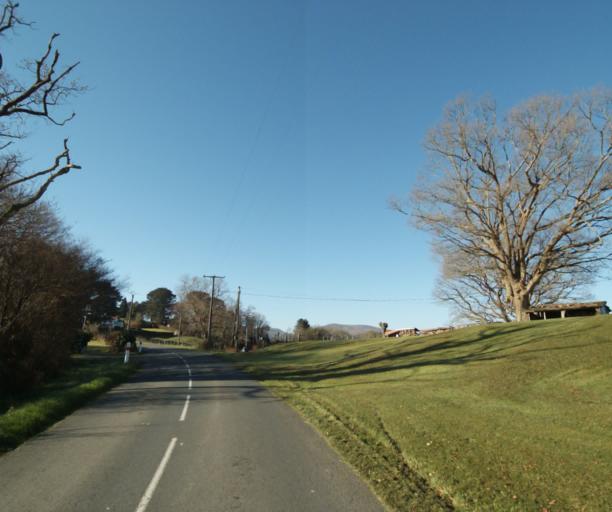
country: FR
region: Aquitaine
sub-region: Departement des Pyrenees-Atlantiques
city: Ciboure
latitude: 43.3567
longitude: -1.6656
